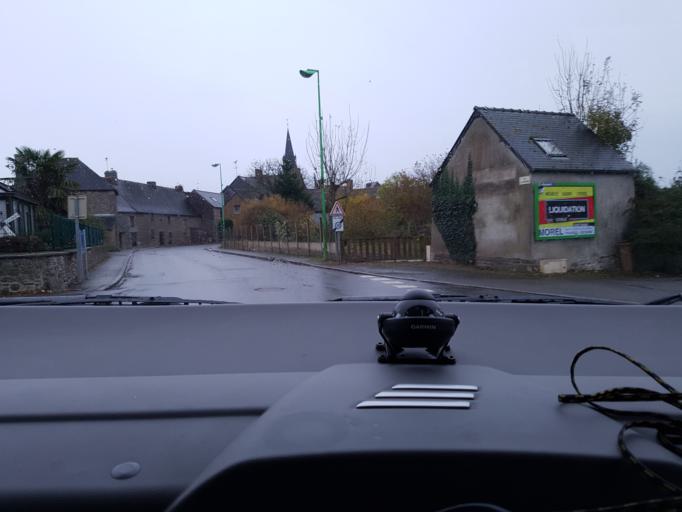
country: FR
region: Brittany
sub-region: Departement d'Ille-et-Vilaine
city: Saint-Sauveur-des-Landes
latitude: 48.3521
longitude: -1.3588
